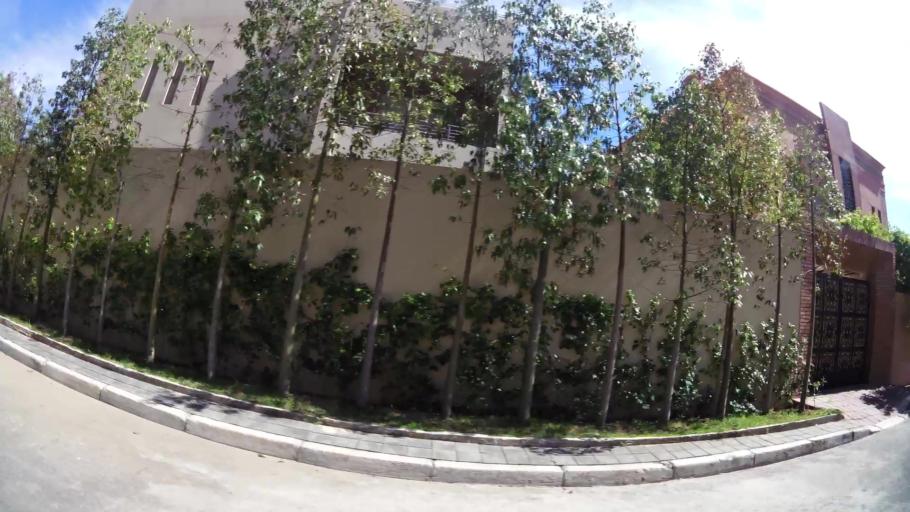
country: MA
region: Marrakech-Tensift-Al Haouz
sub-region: Marrakech
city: Marrakesh
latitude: 31.6415
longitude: -8.0434
